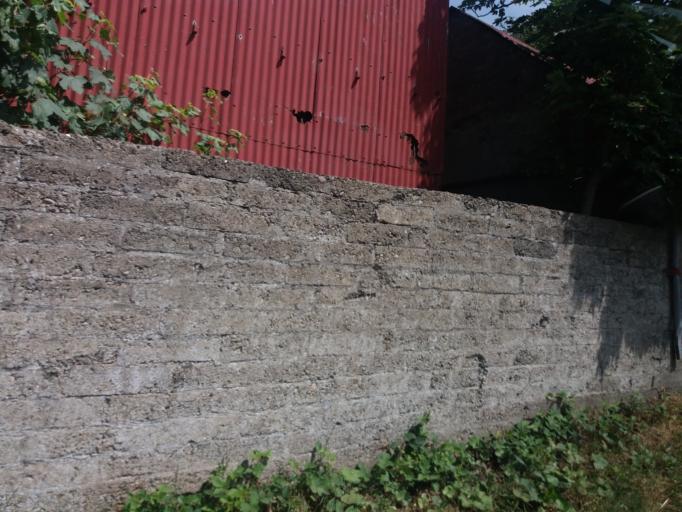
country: IE
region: Leinster
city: Lusk
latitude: 53.5389
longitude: -6.1927
